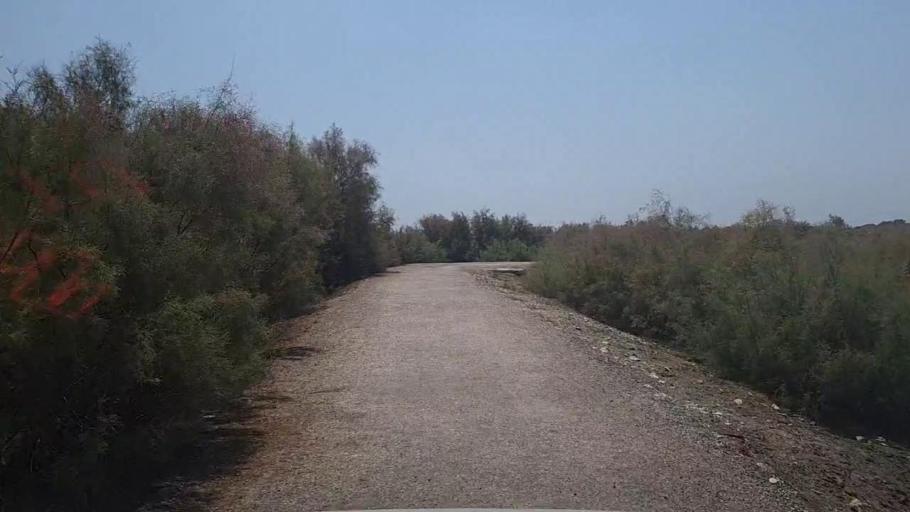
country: PK
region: Sindh
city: Kandhkot
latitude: 28.3032
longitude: 69.3582
